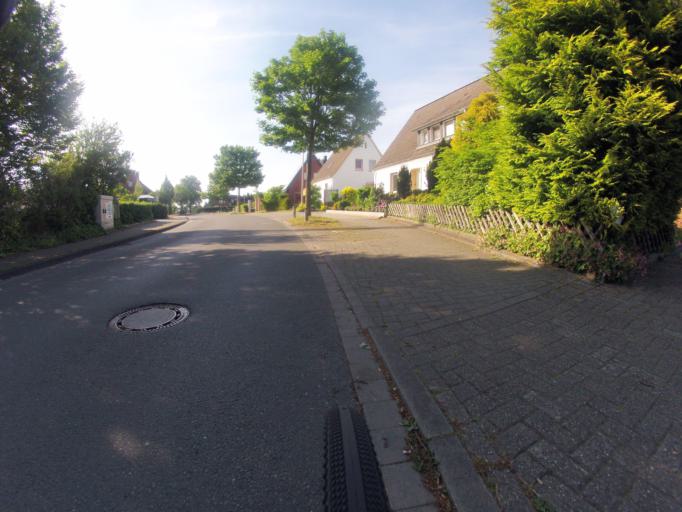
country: DE
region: North Rhine-Westphalia
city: Ibbenburen
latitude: 52.2887
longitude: 7.7142
